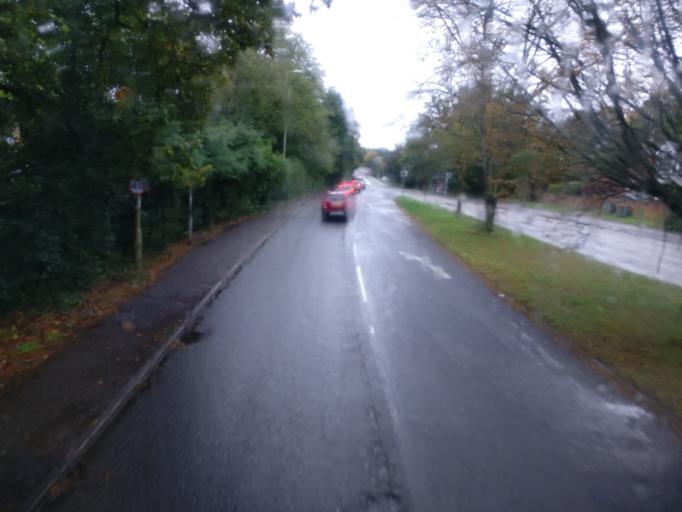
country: GB
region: England
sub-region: Hampshire
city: Farnborough
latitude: 51.3046
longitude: -0.7511
